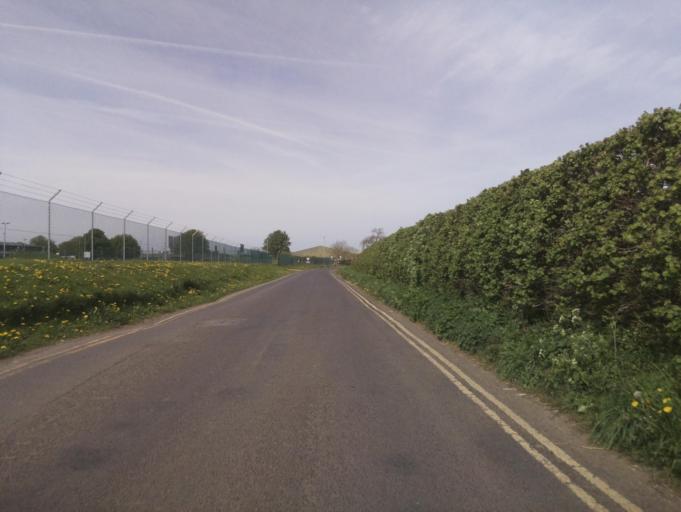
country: GB
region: England
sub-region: Somerset
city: Ilchester
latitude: 51.0163
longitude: -2.6305
